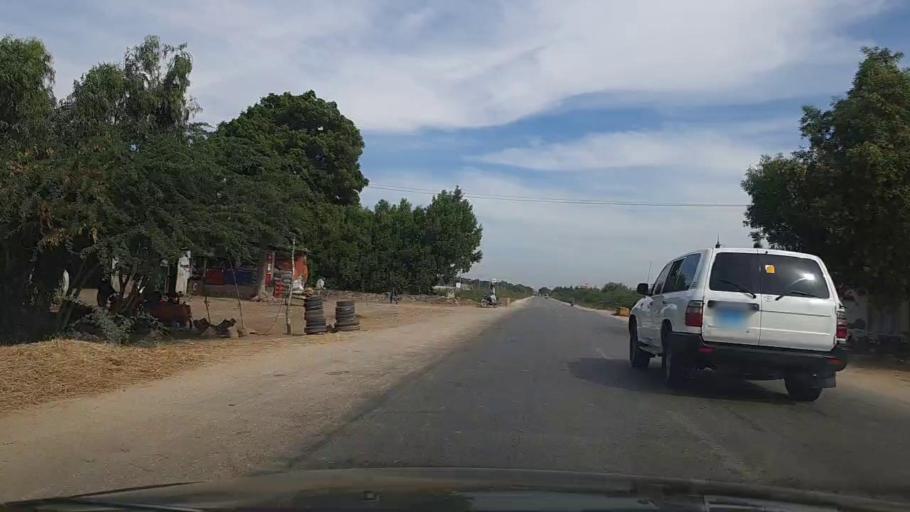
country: PK
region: Sindh
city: Thatta
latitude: 24.7849
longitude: 67.9515
